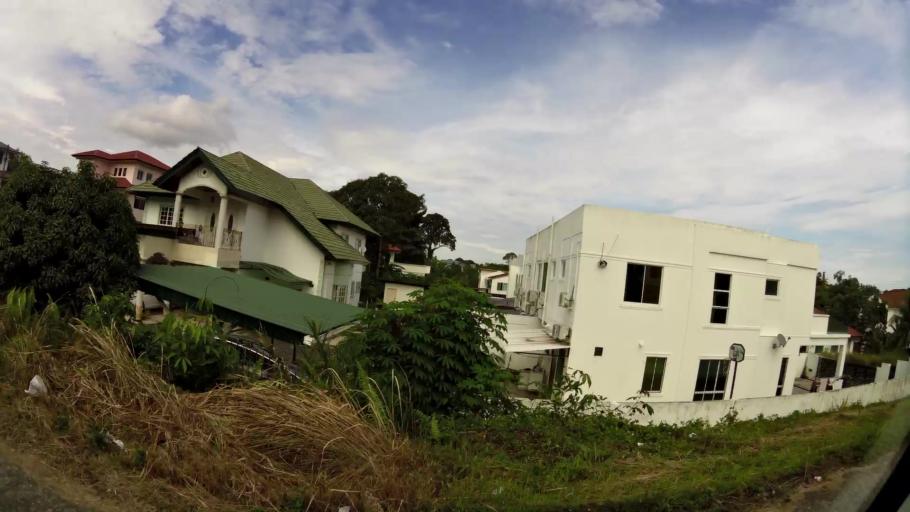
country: BN
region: Brunei and Muara
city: Bandar Seri Begawan
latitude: 4.8994
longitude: 114.8923
